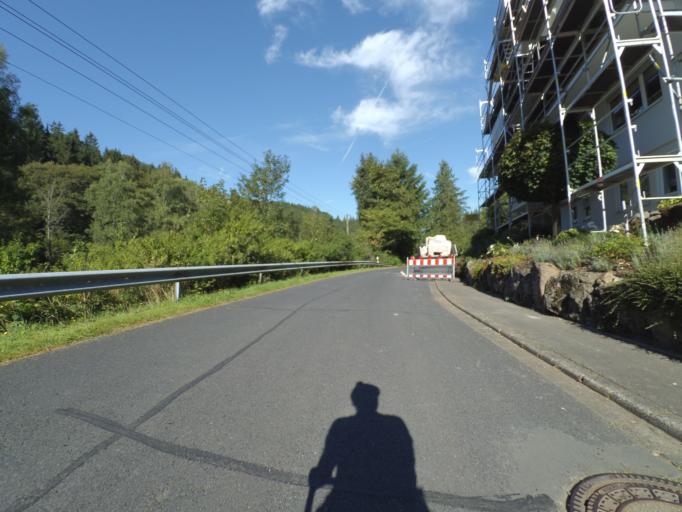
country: DE
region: Rheinland-Pfalz
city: Daun
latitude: 50.1804
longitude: 6.8277
